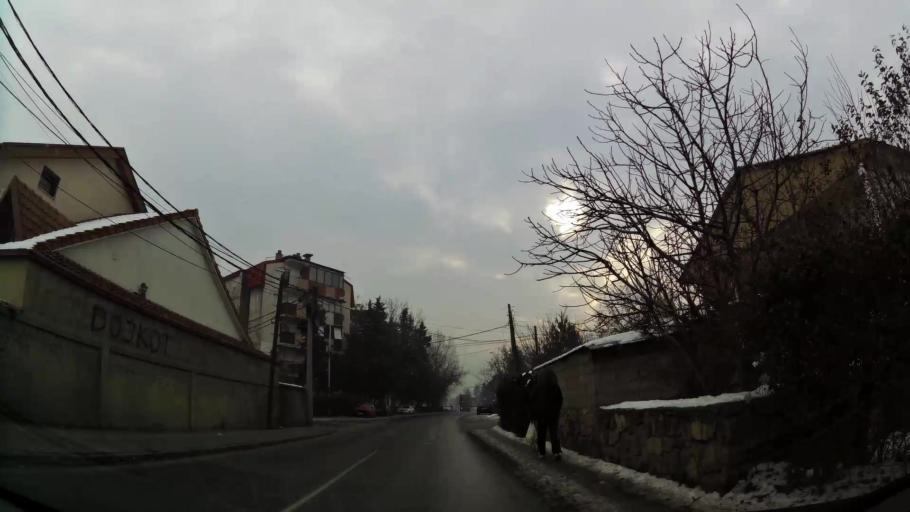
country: MK
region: Saraj
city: Saraj
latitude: 42.0217
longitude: 21.3510
